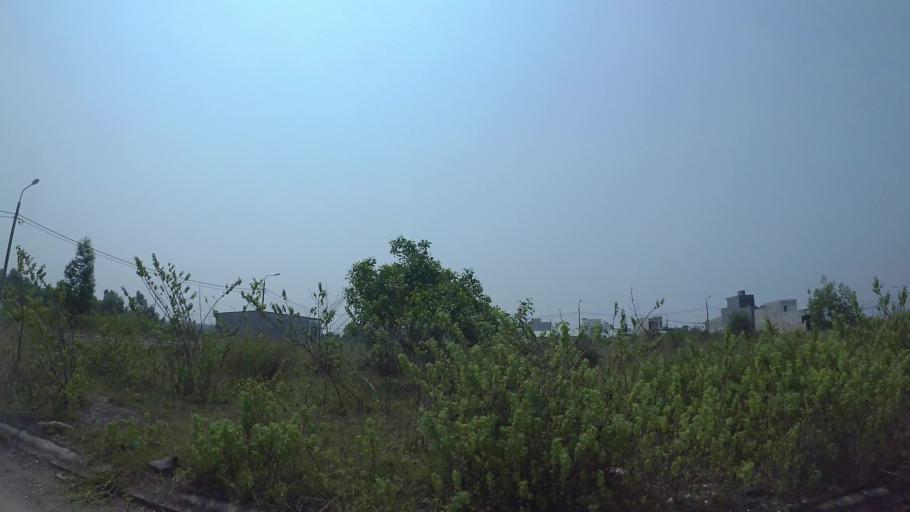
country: VN
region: Da Nang
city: Cam Le
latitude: 15.9815
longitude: 108.2195
